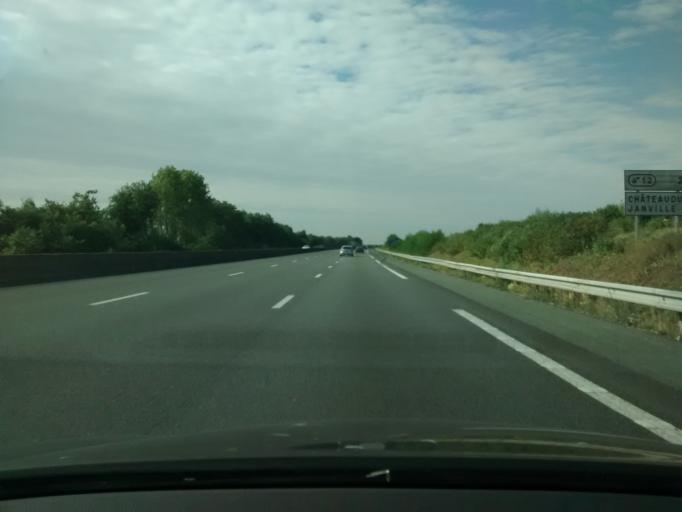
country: FR
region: Ile-de-France
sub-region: Departement de l'Essonne
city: Corbreuse
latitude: 48.4508
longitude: 1.9109
